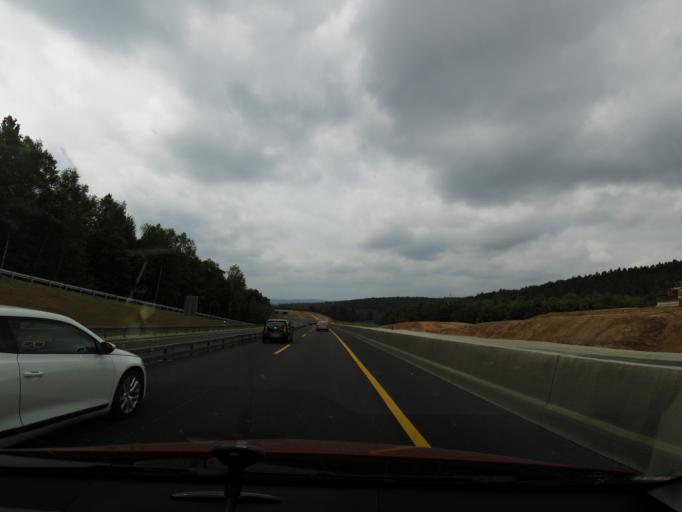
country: DE
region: Hesse
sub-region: Regierungsbezirk Kassel
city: Friedewald
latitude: 50.8860
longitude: 9.8166
